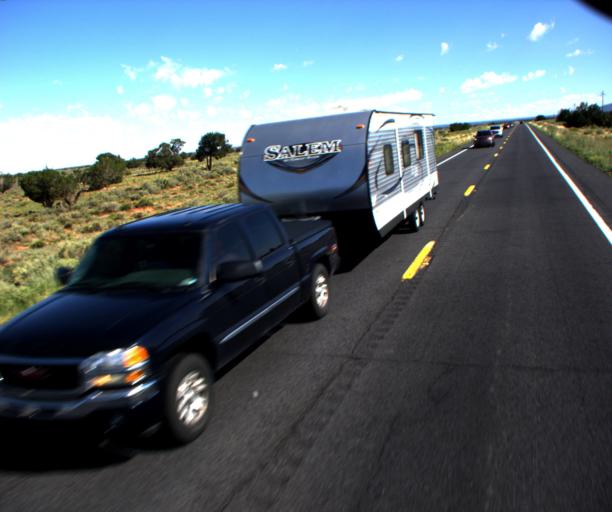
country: US
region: Arizona
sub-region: Coconino County
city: Grand Canyon Village
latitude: 35.6844
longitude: -112.1350
